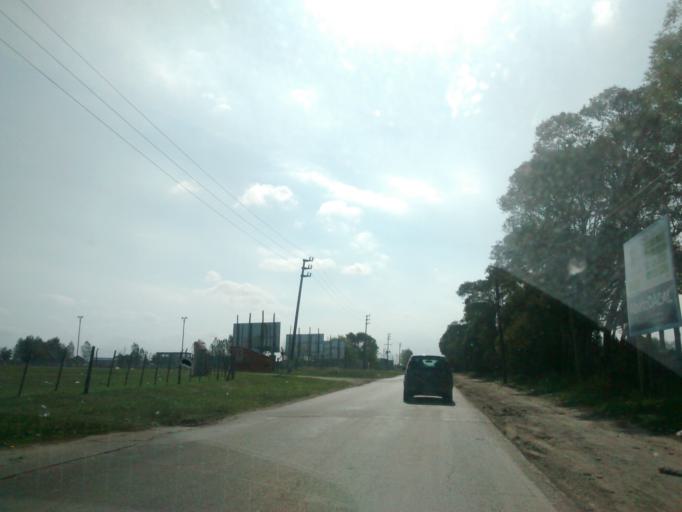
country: AR
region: Buenos Aires
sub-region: Partido de La Plata
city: La Plata
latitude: -34.9705
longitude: -57.8757
